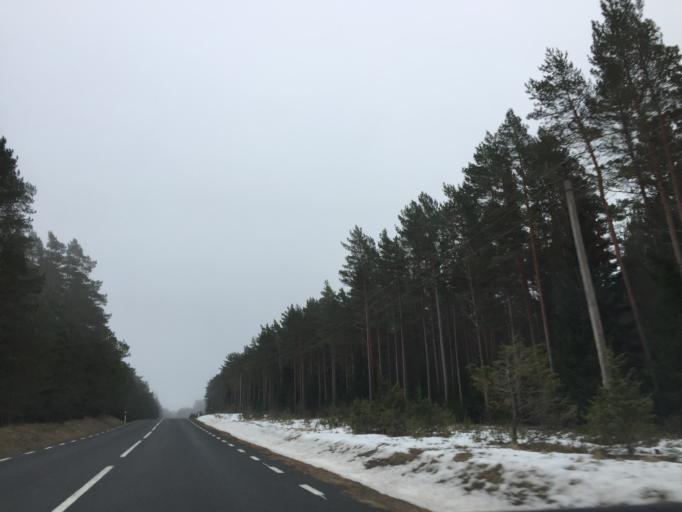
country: EE
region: Saare
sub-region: Kuressaare linn
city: Kuressaare
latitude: 58.4685
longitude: 22.0358
